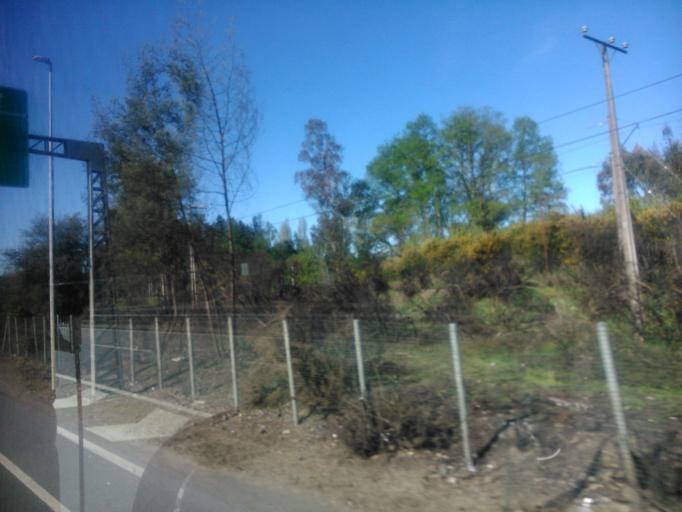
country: CL
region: Araucania
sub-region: Provincia de Cautin
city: Temuco
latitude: -38.7893
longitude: -72.6163
